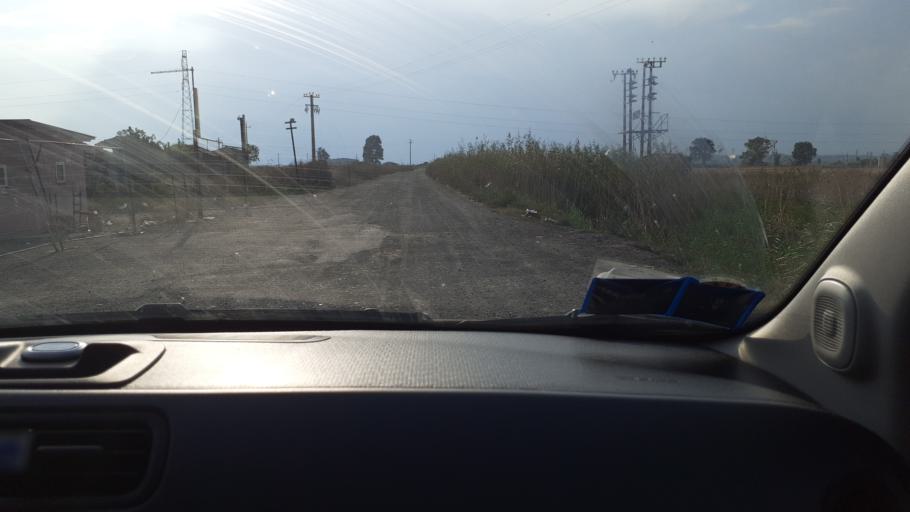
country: IT
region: Sicily
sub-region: Catania
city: Misterbianco
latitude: 37.4338
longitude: 15.0079
